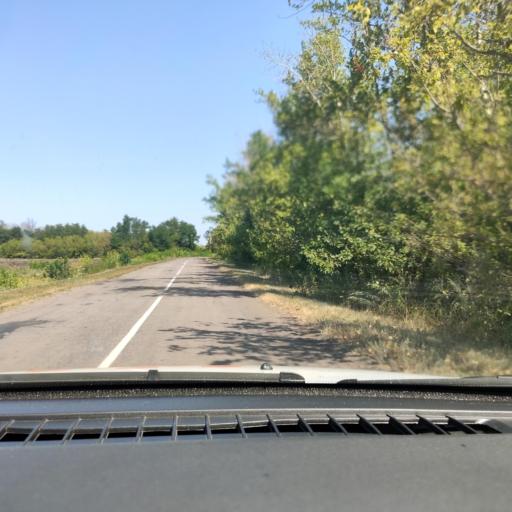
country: RU
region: Voronezj
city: Ostrogozhsk
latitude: 50.7111
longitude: 39.3379
